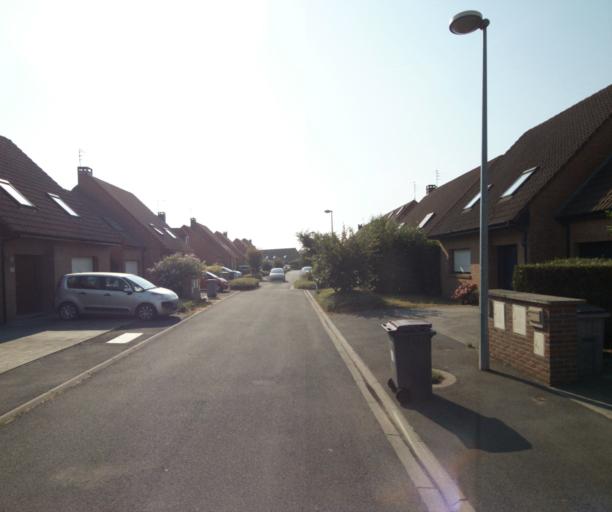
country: FR
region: Nord-Pas-de-Calais
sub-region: Departement du Nord
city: Quesnoy-sur-Deule
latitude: 50.7207
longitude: 3.0006
